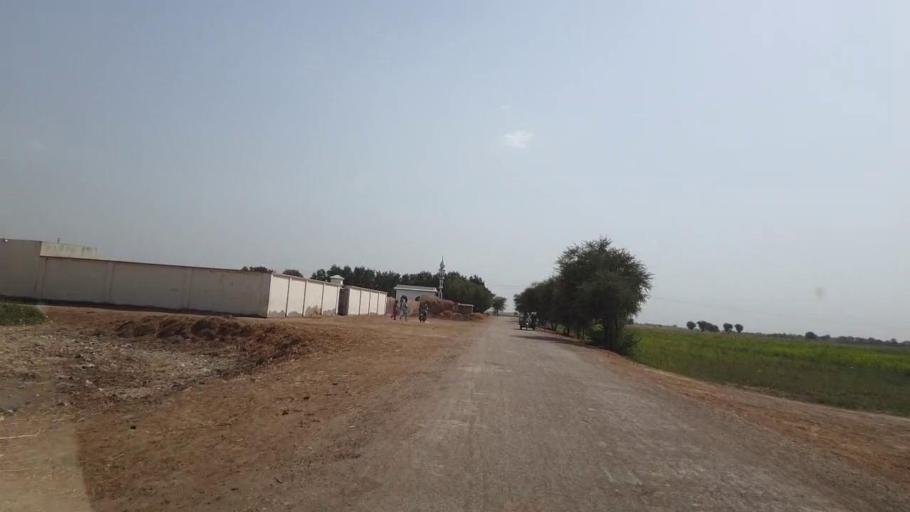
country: PK
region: Sindh
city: Rajo Khanani
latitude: 25.0487
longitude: 68.8768
